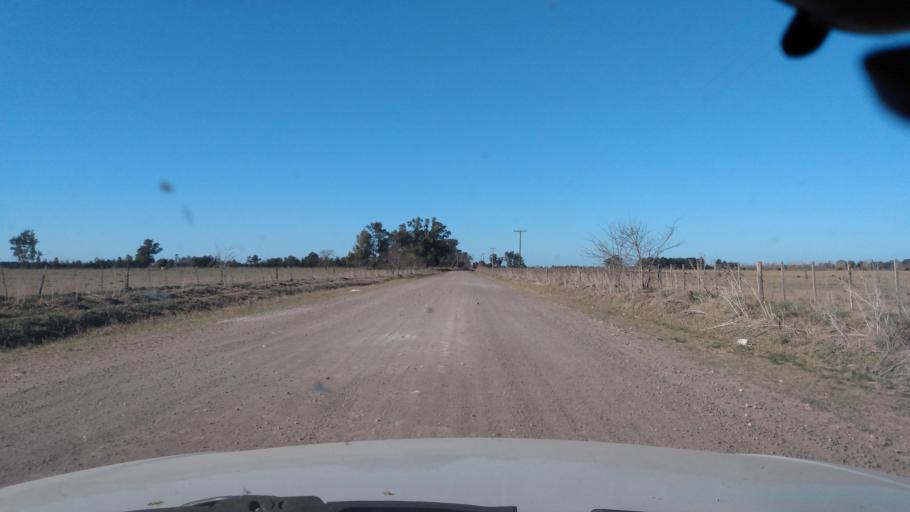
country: AR
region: Buenos Aires
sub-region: Partido de Mercedes
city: Mercedes
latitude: -34.6099
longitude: -59.3152
